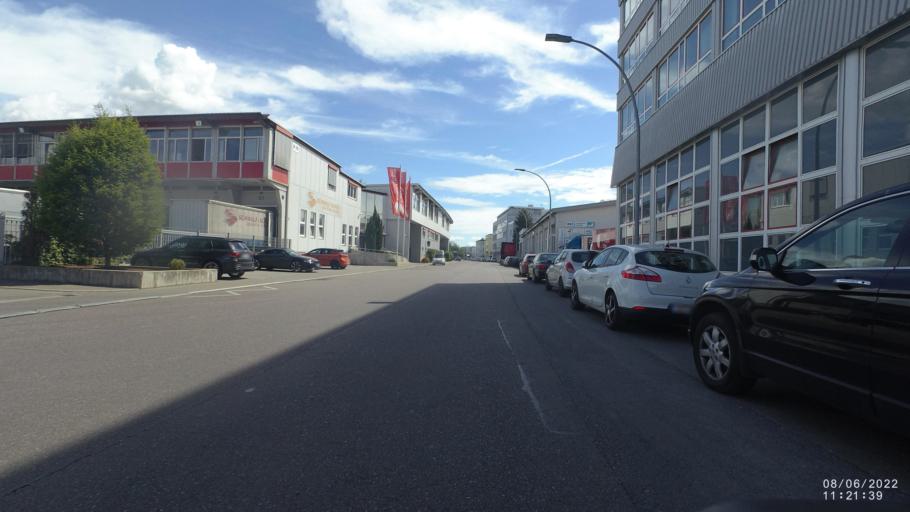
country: DE
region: Baden-Wuerttemberg
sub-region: Regierungsbezirk Stuttgart
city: Fellbach
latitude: 48.8207
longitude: 9.2760
